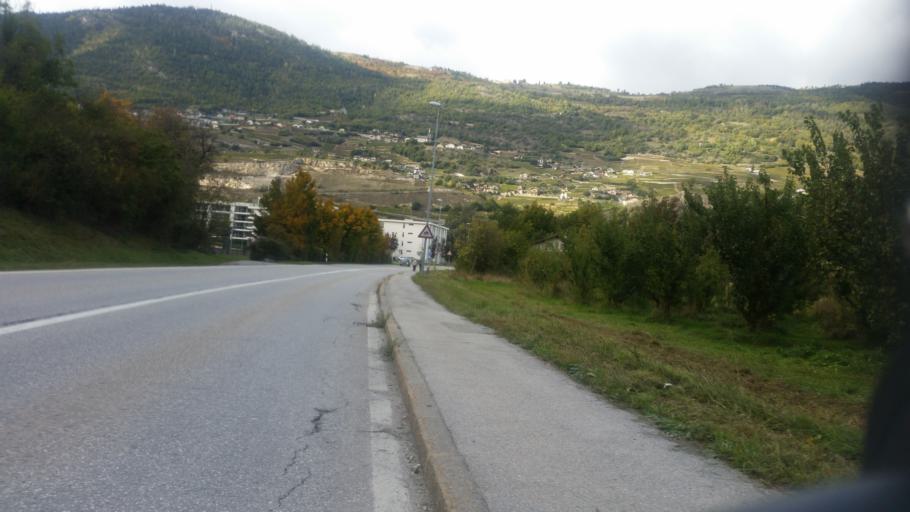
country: CH
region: Valais
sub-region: Sierre District
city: Grone
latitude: 46.2593
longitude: 7.4659
